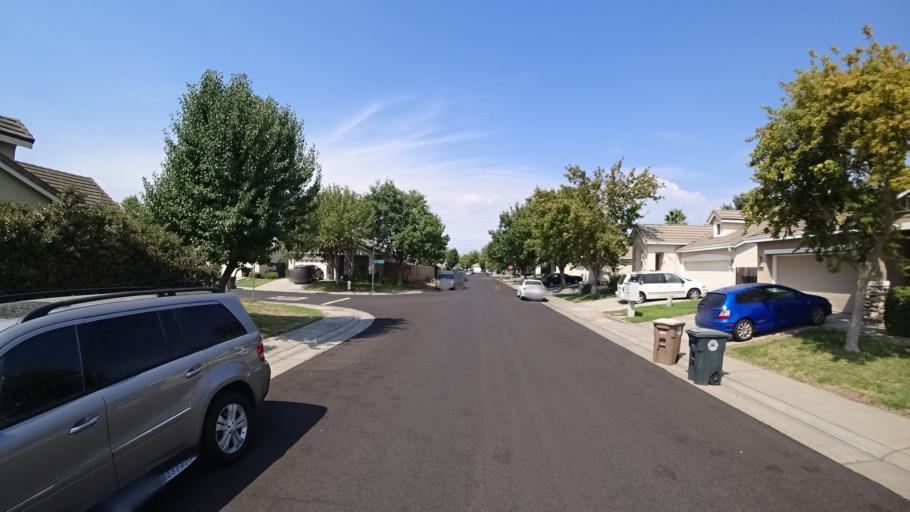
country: US
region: California
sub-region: Sacramento County
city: Laguna
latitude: 38.3933
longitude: -121.4478
